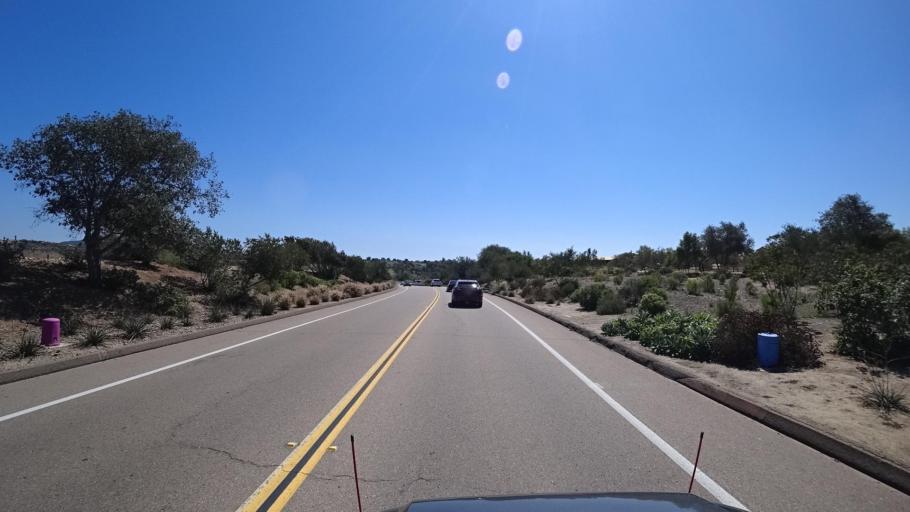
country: US
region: California
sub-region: San Diego County
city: Fairbanks Ranch
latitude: 32.9997
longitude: -117.1588
